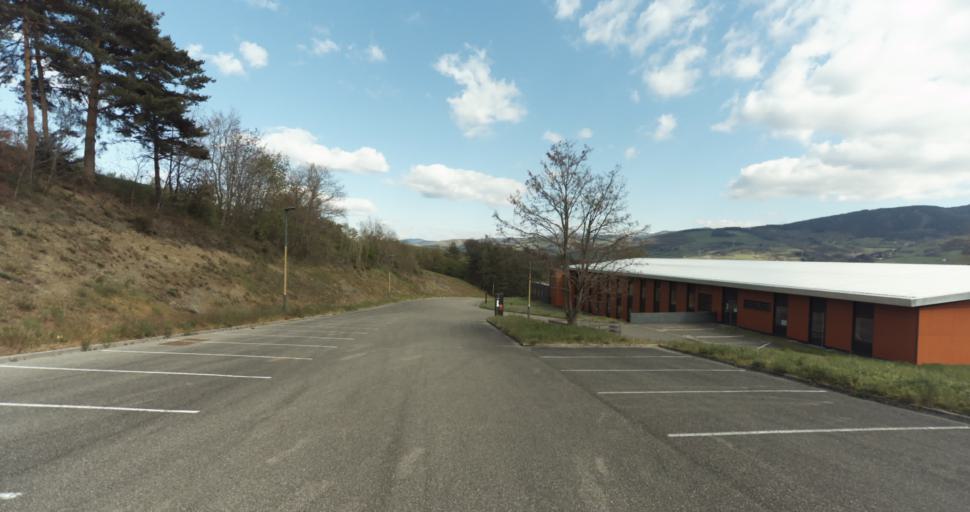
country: FR
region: Rhone-Alpes
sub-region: Departement de la Loire
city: Saint-Jean-Bonnefonds
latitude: 45.4593
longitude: 4.4567
